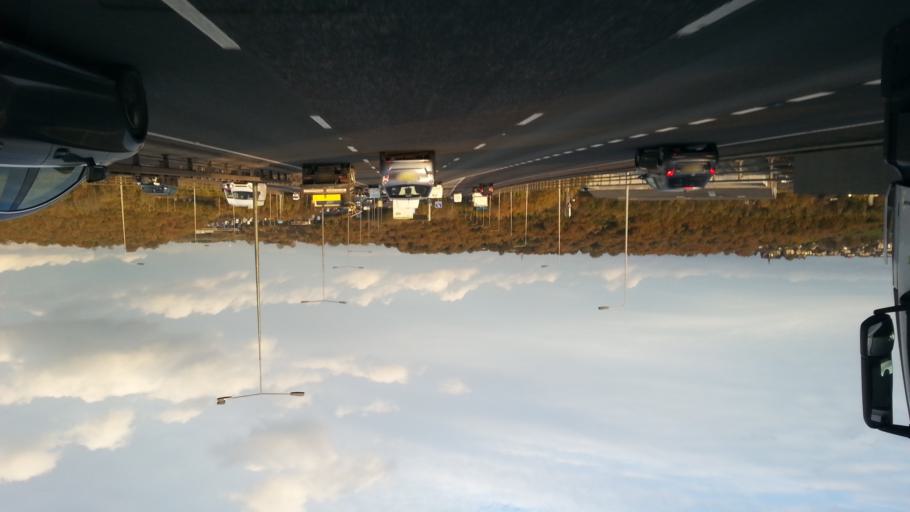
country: GB
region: England
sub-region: Calderdale
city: Brighouse
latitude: 53.6914
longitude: -1.7575
